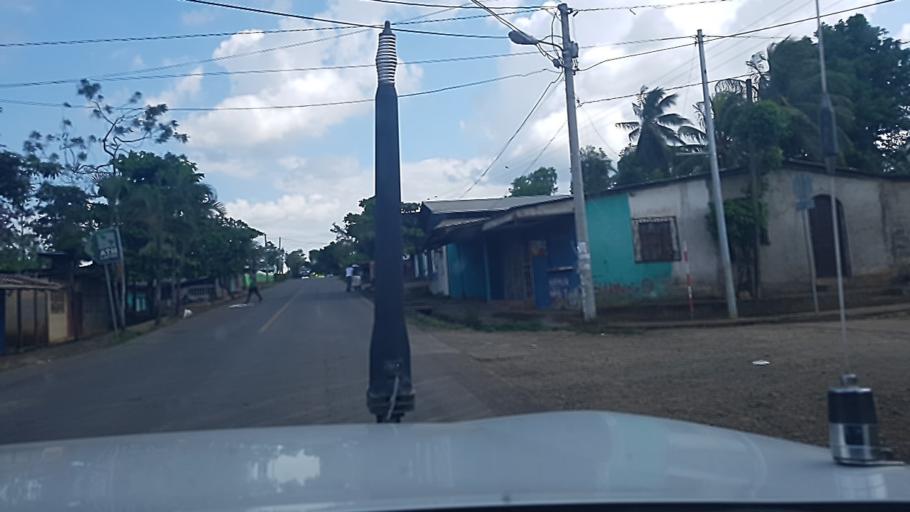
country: NI
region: Atlantico Sur
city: Nueva Guinea
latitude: 11.6901
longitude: -84.4616
